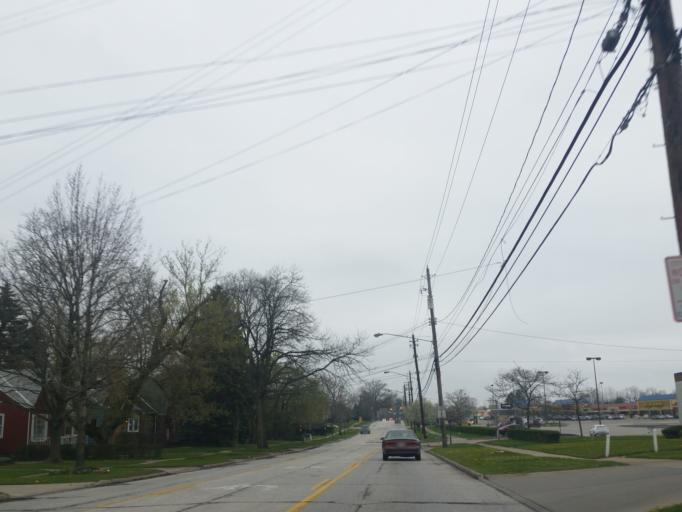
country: US
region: Ohio
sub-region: Cuyahoga County
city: Brooklyn
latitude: 41.4304
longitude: -81.7296
